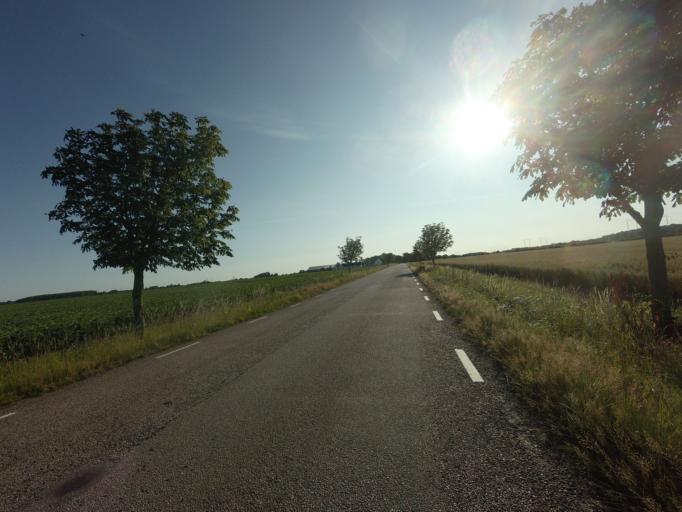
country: SE
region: Skane
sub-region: Hoganas Kommun
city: Hoganas
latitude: 56.1361
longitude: 12.5966
